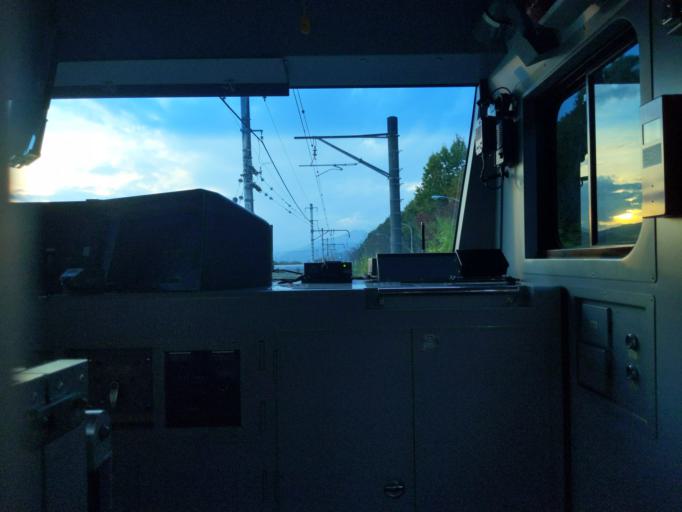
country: JP
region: Tokyo
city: Fussa
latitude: 35.7293
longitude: 139.2749
